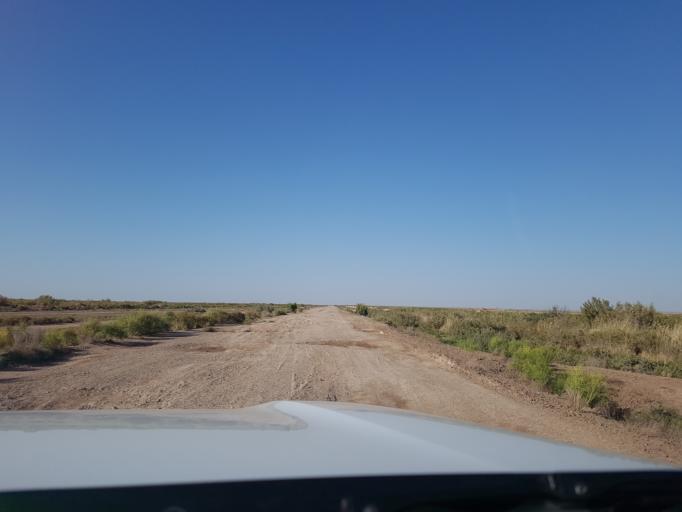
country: IR
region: Razavi Khorasan
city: Sarakhs
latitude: 36.9647
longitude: 61.3830
